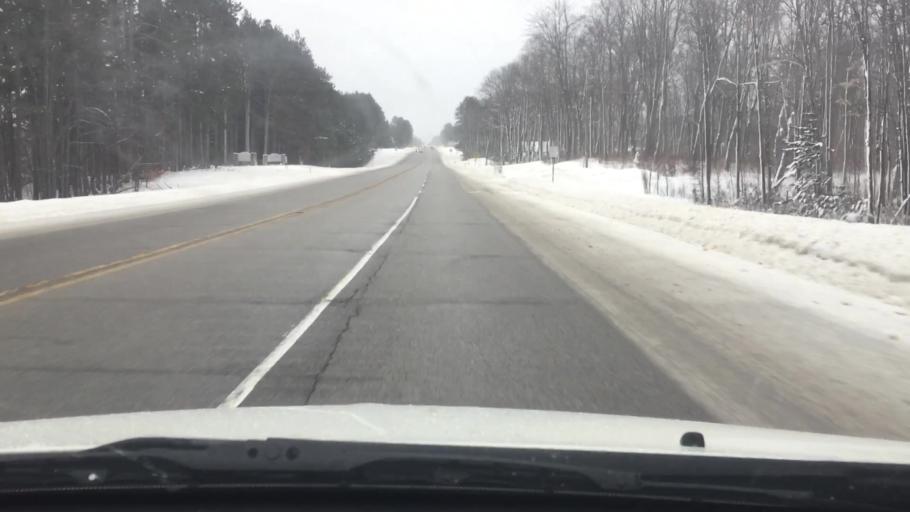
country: US
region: Michigan
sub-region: Otsego County
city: Gaylord
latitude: 45.0385
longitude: -84.7758
